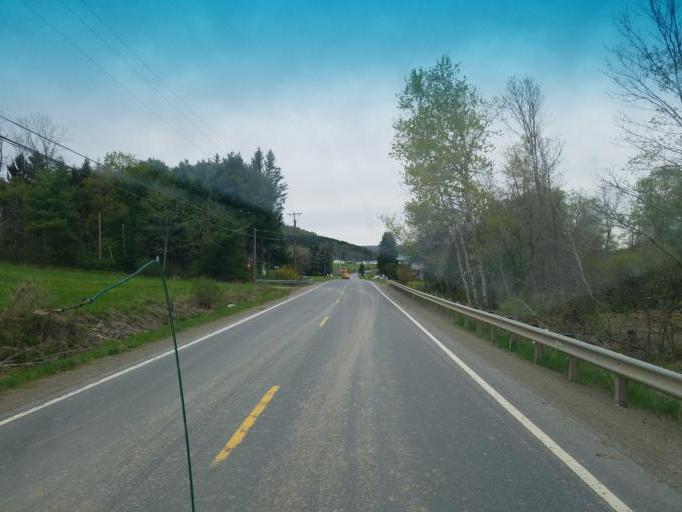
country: US
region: Pennsylvania
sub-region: Tioga County
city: Westfield
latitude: 41.8894
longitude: -77.5294
